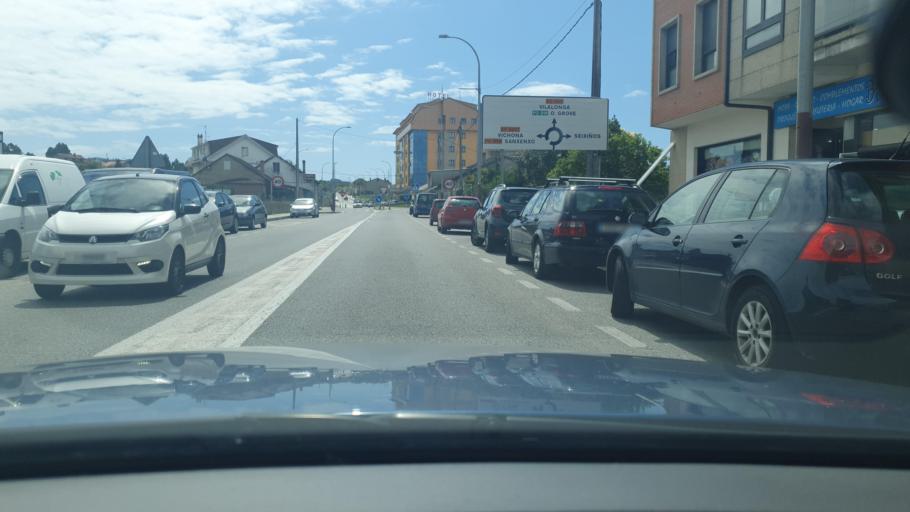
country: ES
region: Galicia
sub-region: Provincia de Pontevedra
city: Meano
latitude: 42.4486
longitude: -8.8171
